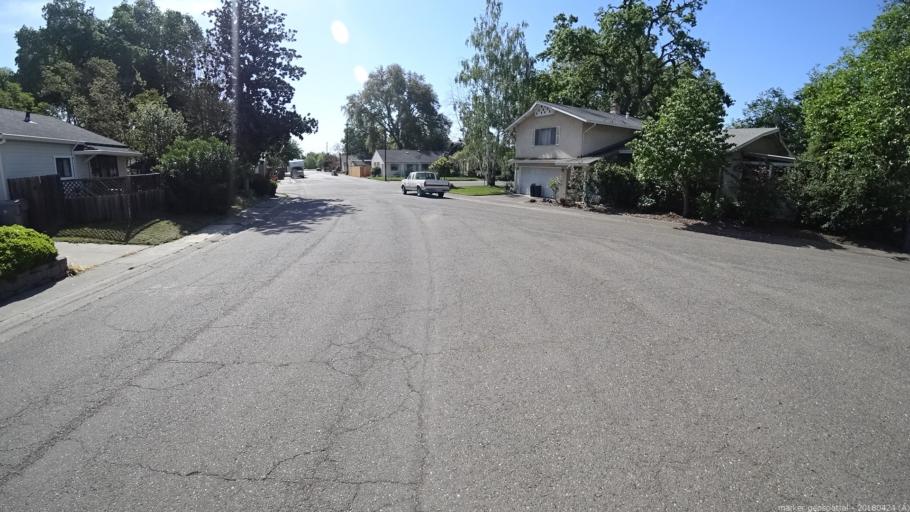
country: US
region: California
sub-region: Yolo County
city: West Sacramento
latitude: 38.5666
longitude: -121.5300
